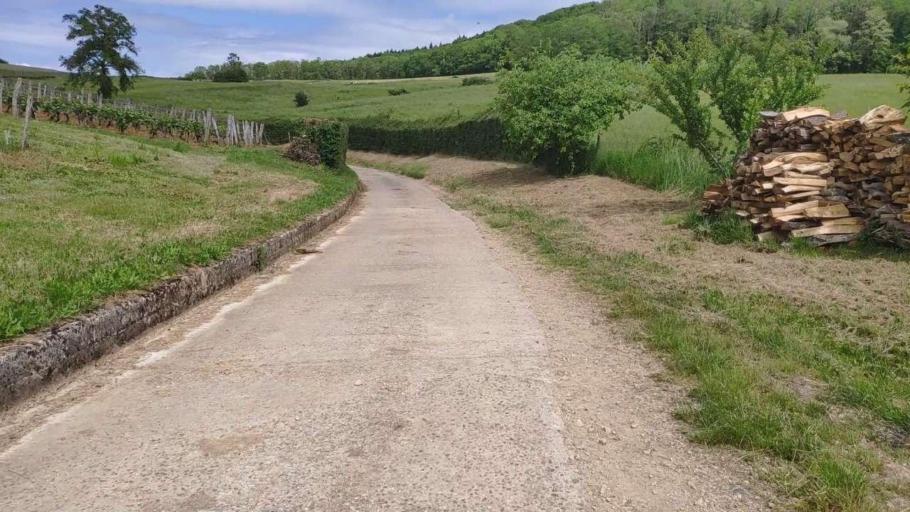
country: FR
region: Franche-Comte
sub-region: Departement du Jura
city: Montmorot
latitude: 46.7352
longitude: 5.5343
